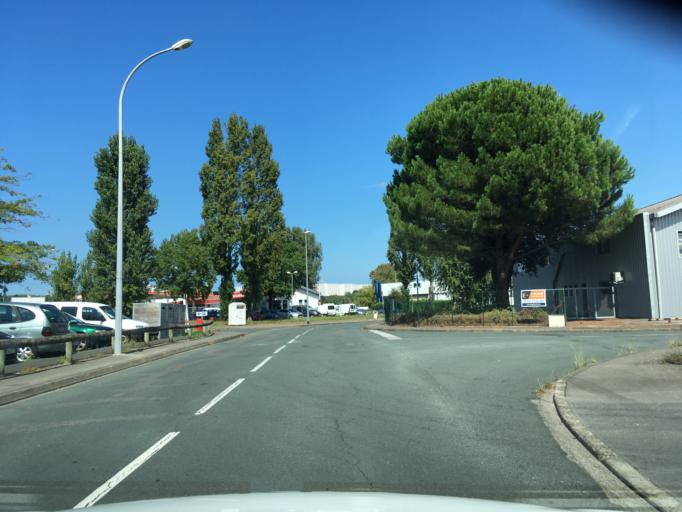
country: FR
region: Aquitaine
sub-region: Departement des Pyrenees-Atlantiques
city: Bayonne
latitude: 43.4884
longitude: -1.4564
